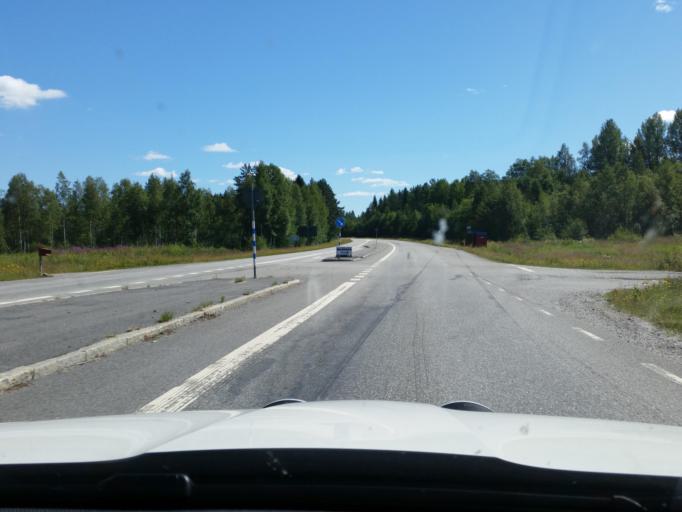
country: SE
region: Norrbotten
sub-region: Pitea Kommun
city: Bergsviken
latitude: 65.3178
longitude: 21.2901
